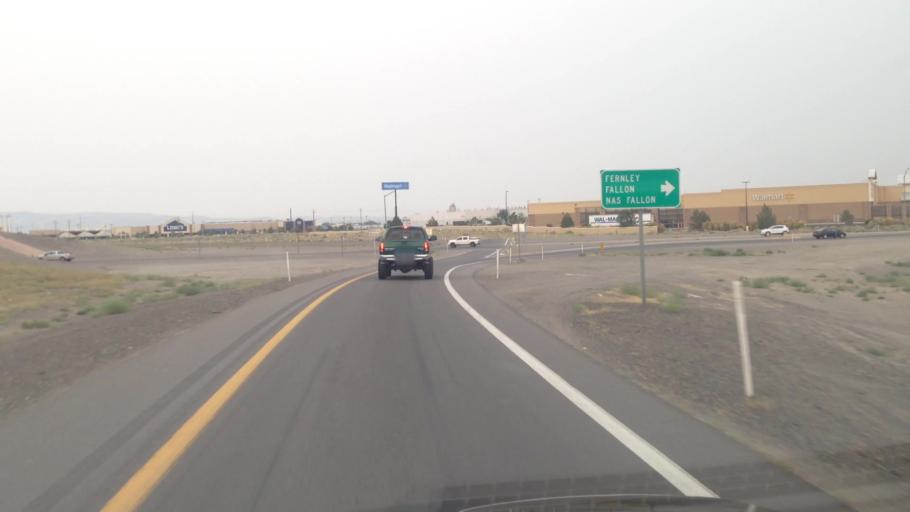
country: US
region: Nevada
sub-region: Lyon County
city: Fernley
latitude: 39.6125
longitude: -119.2203
